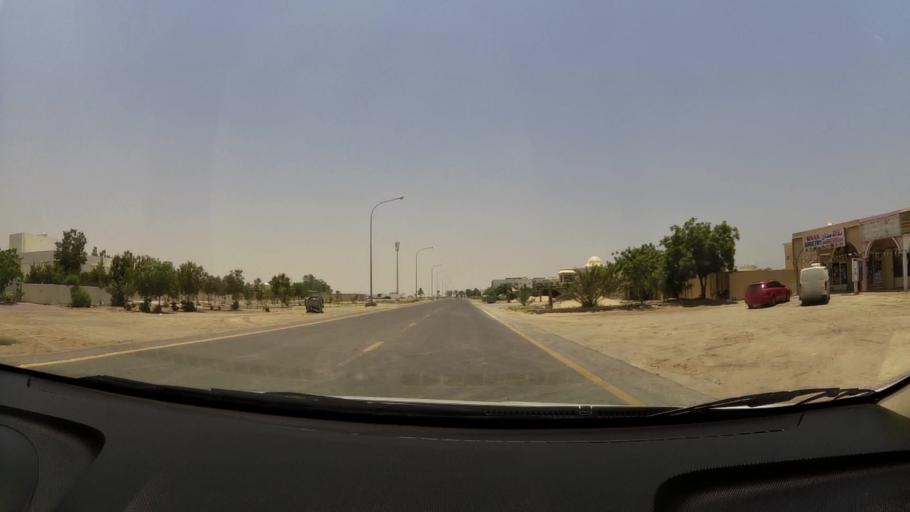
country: AE
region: Umm al Qaywayn
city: Umm al Qaywayn
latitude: 25.5343
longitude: 55.5422
